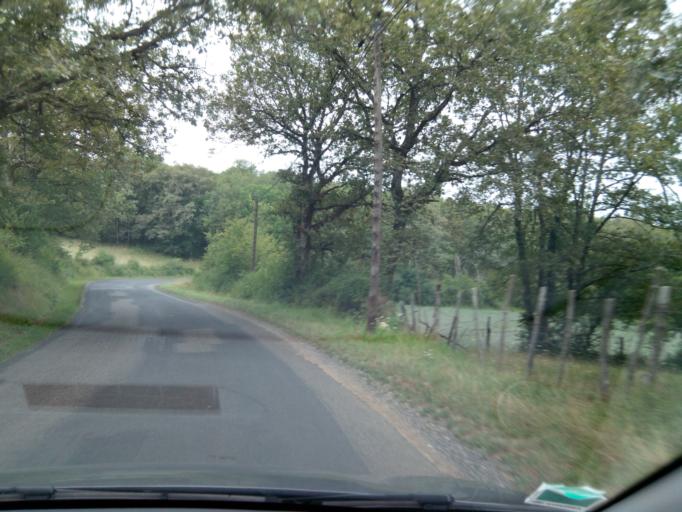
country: FR
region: Limousin
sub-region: Departement de la Correze
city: Cosnac
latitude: 45.0171
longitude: 1.5447
